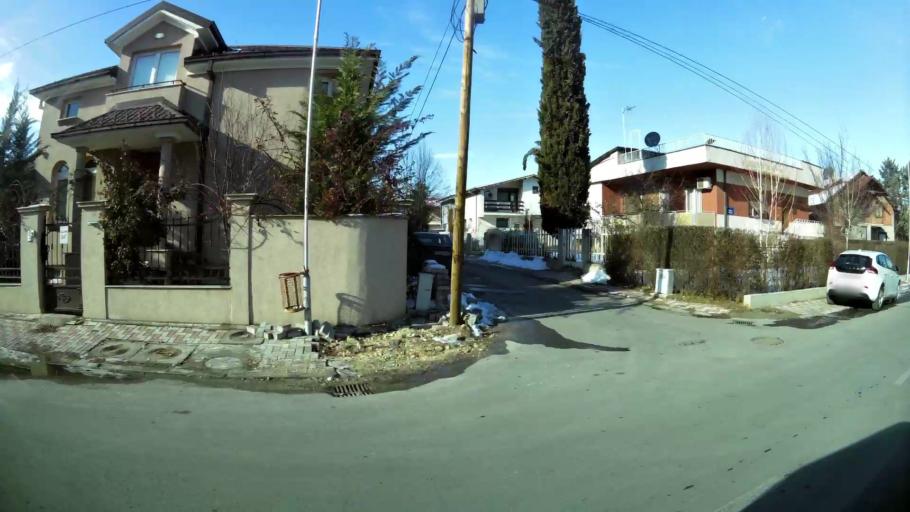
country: MK
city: Krushopek
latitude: 42.0080
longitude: 21.3773
